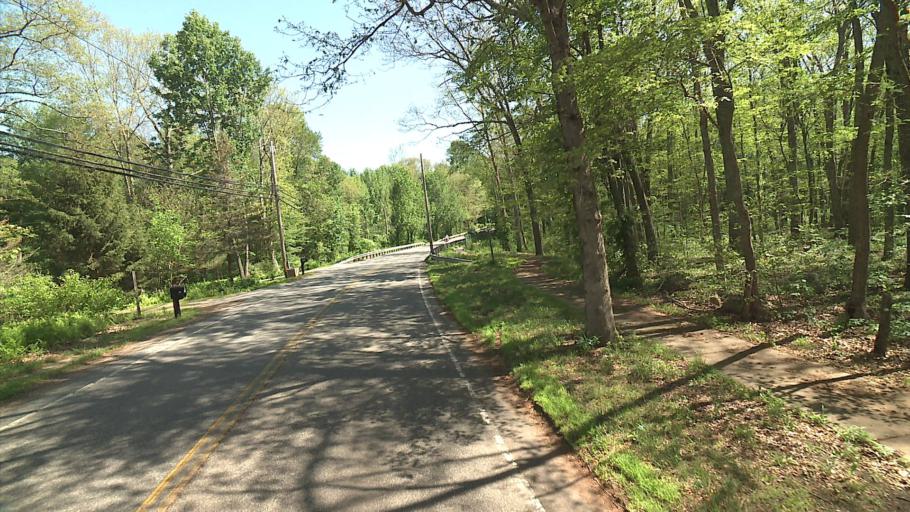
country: US
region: Connecticut
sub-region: New London County
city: Colchester
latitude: 41.5923
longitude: -72.3041
